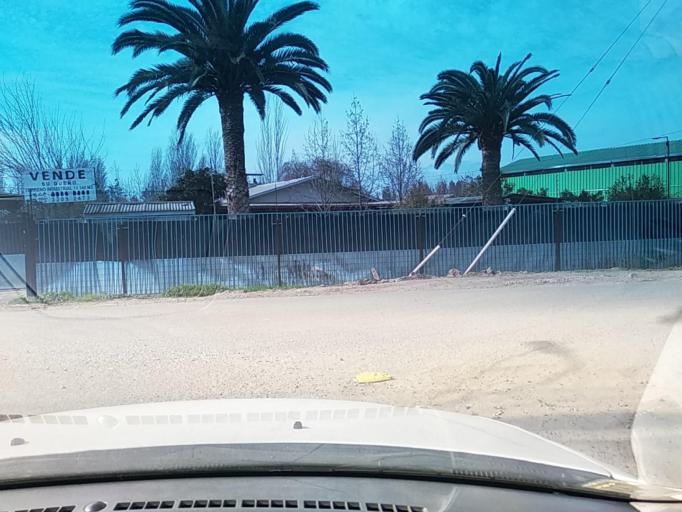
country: CL
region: Santiago Metropolitan
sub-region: Provincia de Chacabuco
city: Chicureo Abajo
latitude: -33.2846
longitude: -70.7303
